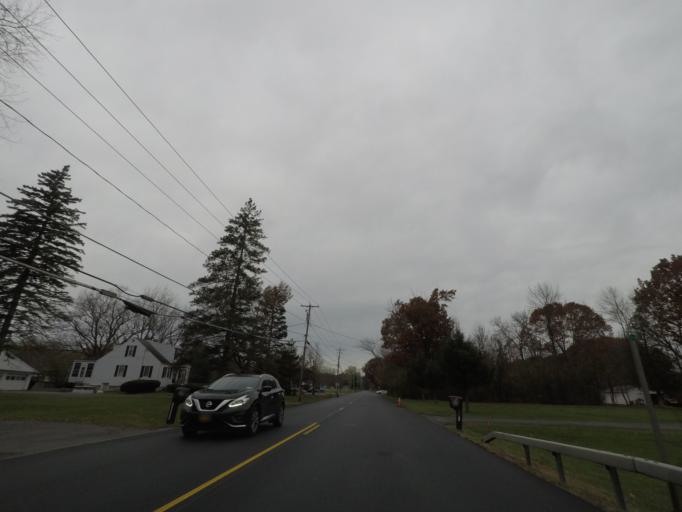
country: US
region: New York
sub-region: Saratoga County
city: Waterford
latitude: 42.8360
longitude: -73.6707
